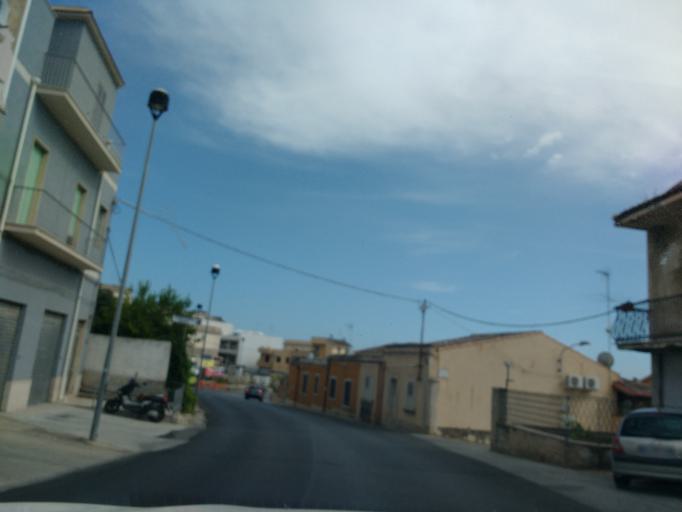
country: IT
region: Sicily
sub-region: Provincia di Siracusa
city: Noto
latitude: 36.8897
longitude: 15.0624
